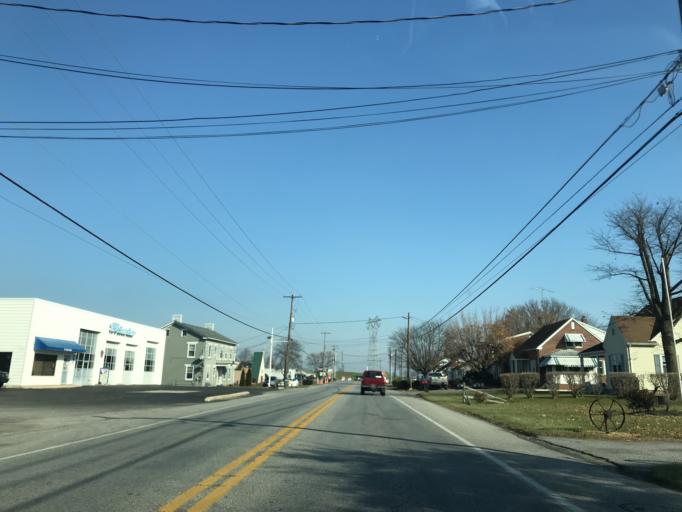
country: US
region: Pennsylvania
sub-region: Adams County
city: Mount Pleasant
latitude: 39.7527
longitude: -77.0680
